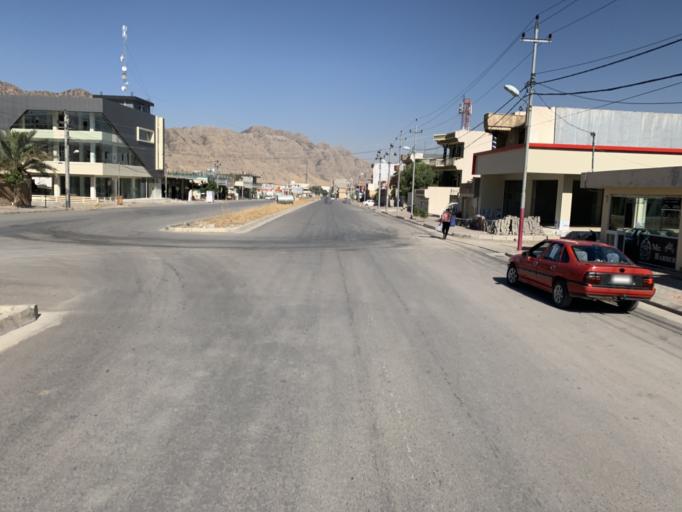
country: IQ
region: As Sulaymaniyah
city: Raniye
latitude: 36.2581
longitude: 44.8696
